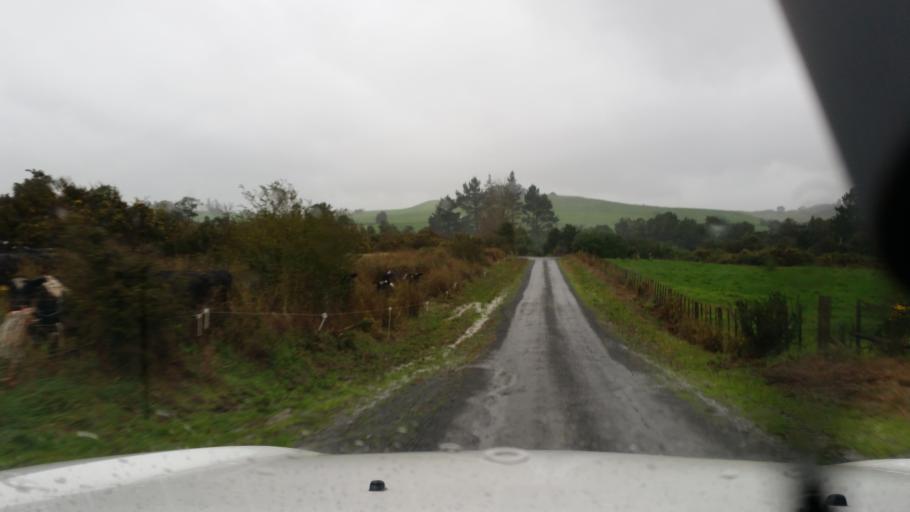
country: NZ
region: Northland
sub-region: Whangarei
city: Maungatapere
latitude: -35.7446
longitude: 174.0832
